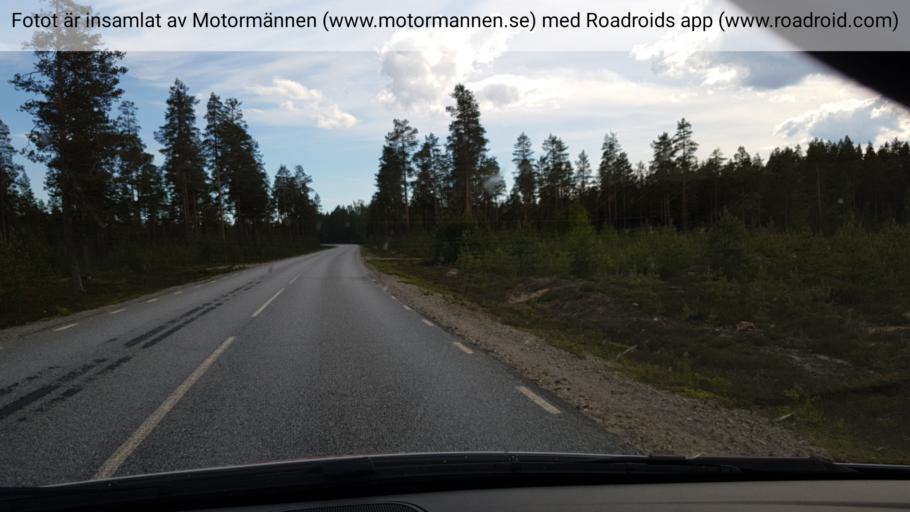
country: SE
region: Vaesterbotten
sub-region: Umea Kommun
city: Saevar
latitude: 63.9695
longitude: 20.5076
